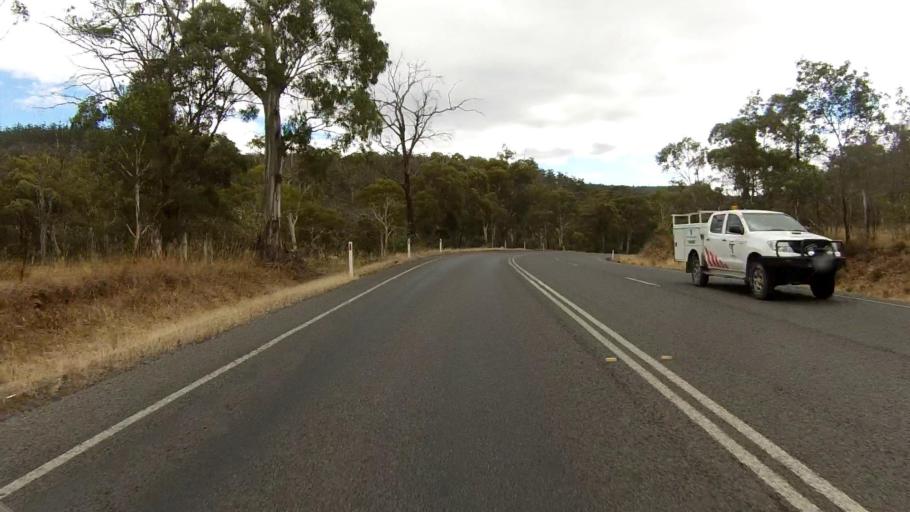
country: AU
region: Tasmania
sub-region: Sorell
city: Sorell
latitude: -42.5725
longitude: 147.8206
